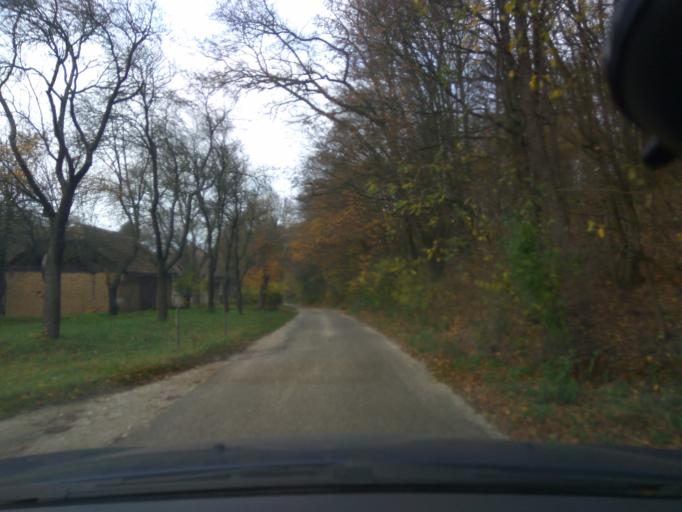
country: SK
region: Trnavsky
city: Vrbove
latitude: 48.6912
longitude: 17.6948
